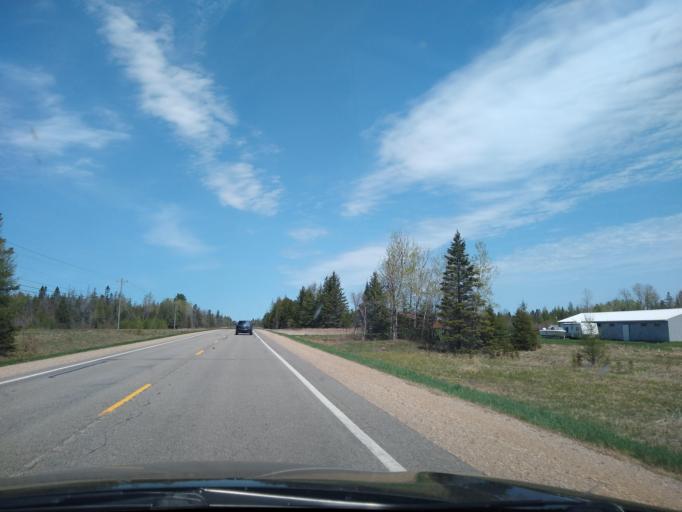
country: US
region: Michigan
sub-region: Delta County
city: Gladstone
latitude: 45.9464
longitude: -86.9720
